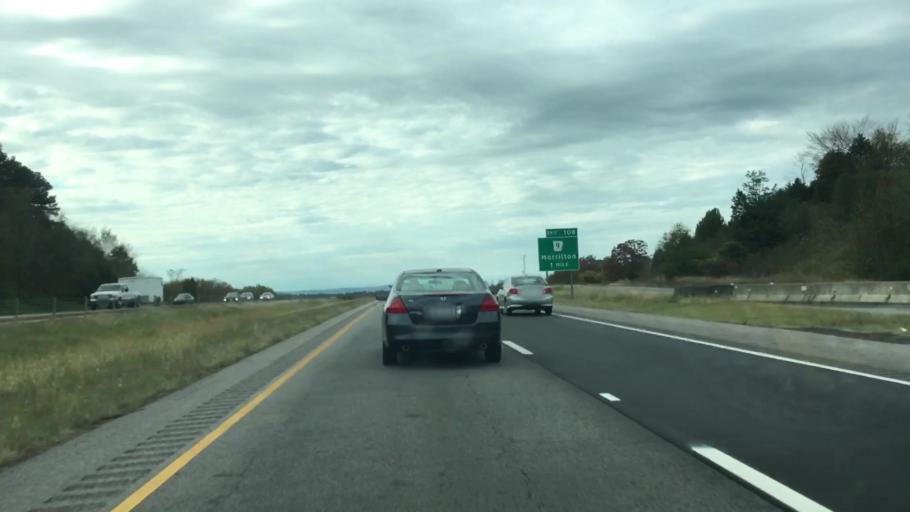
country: US
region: Arkansas
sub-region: Conway County
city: Morrilton
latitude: 35.1708
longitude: -92.6952
